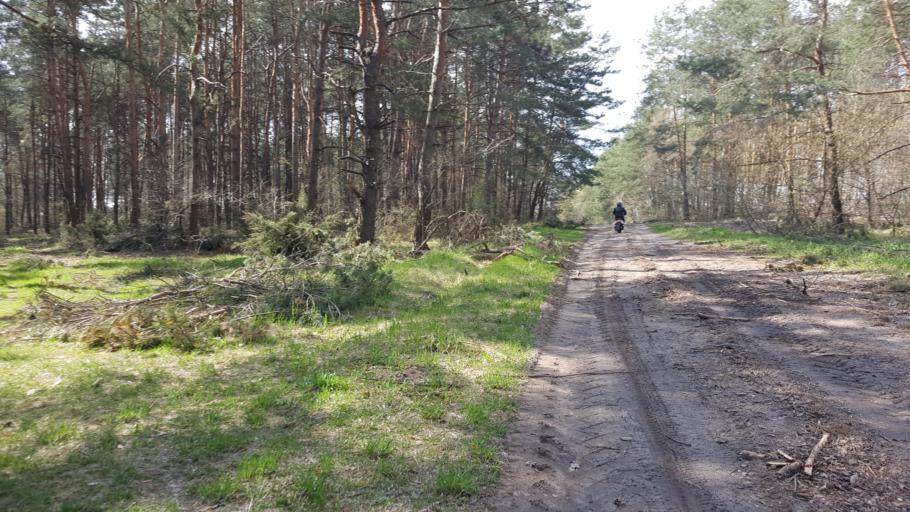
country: BY
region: Brest
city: Kamyanyets
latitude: 52.3335
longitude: 23.9203
